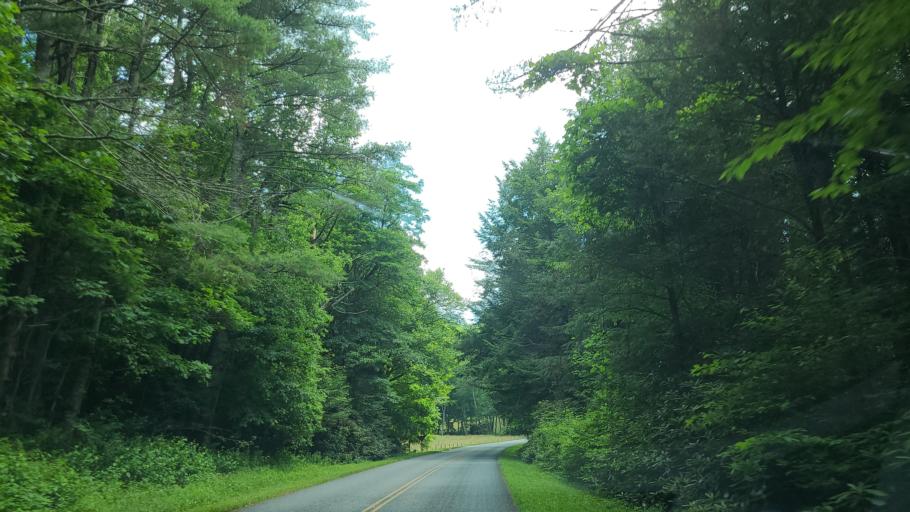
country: US
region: North Carolina
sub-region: Avery County
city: Newland
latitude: 35.9866
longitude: -81.9094
